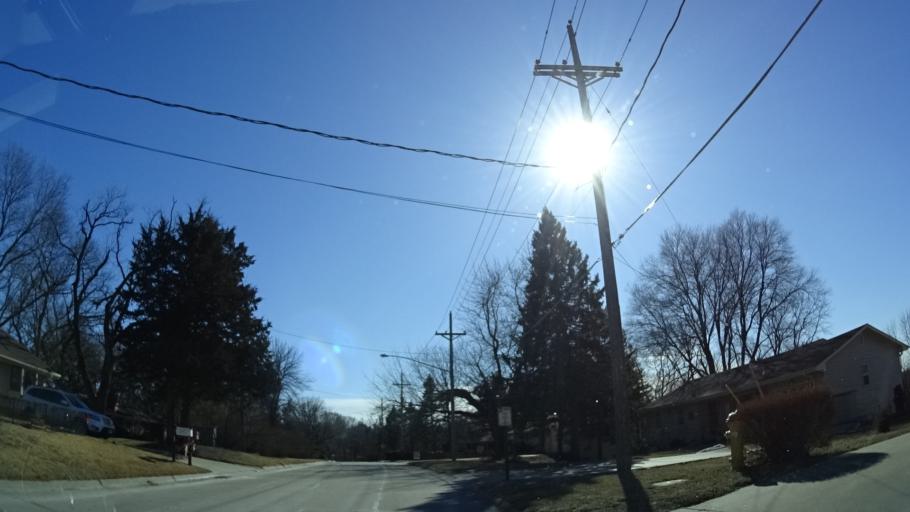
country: US
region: Nebraska
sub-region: Sarpy County
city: Bellevue
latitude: 41.1498
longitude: -95.9005
